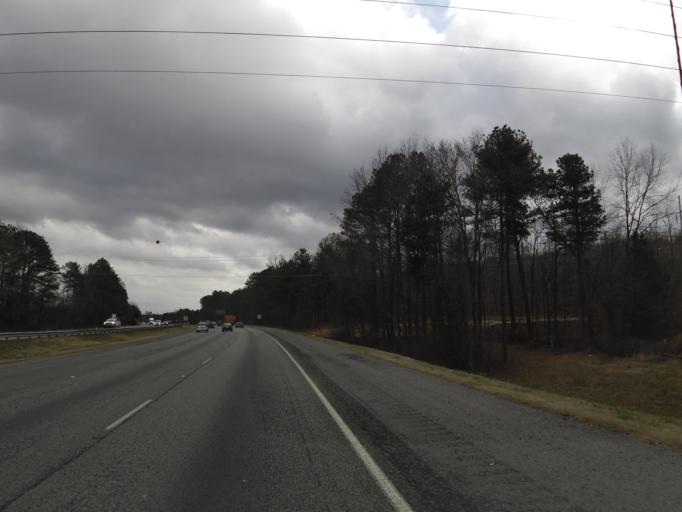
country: US
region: Georgia
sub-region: Whitfield County
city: Dalton
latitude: 34.6705
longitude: -84.9970
